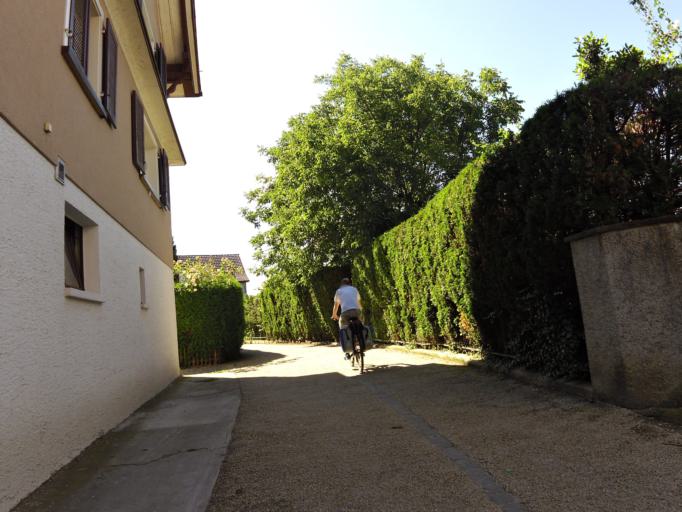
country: CH
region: Thurgau
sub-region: Arbon District
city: Arbon
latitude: 47.5049
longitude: 9.4411
